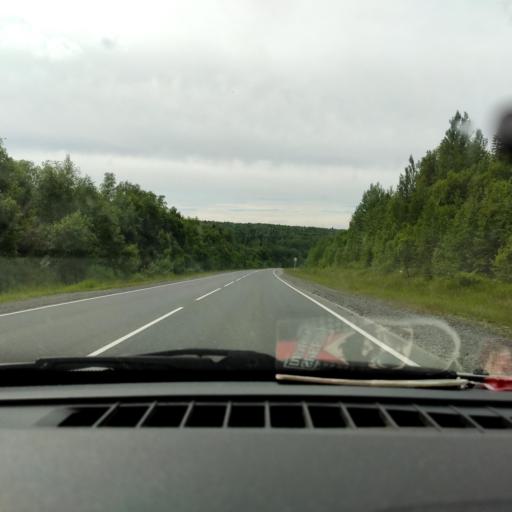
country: RU
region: Perm
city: Pashiya
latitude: 58.3725
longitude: 58.0496
